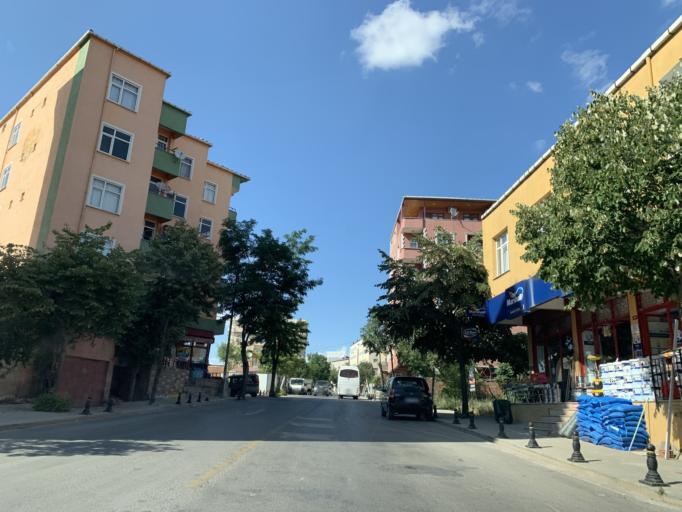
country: TR
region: Istanbul
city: Pendik
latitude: 40.8830
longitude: 29.2825
